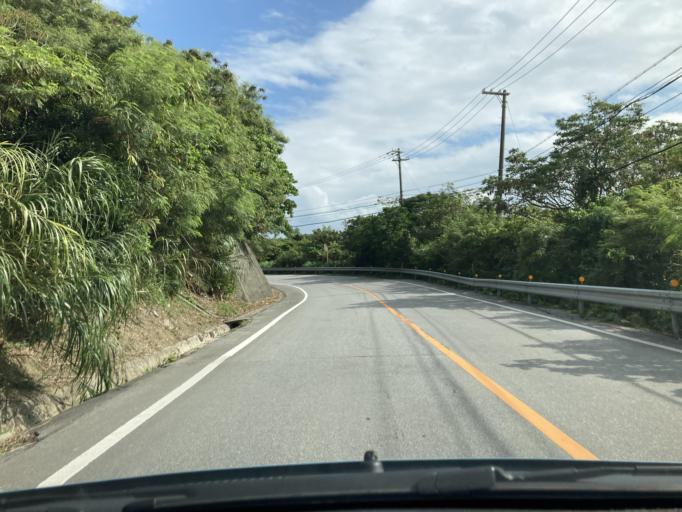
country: JP
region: Okinawa
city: Ginowan
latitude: 26.2695
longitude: 127.7824
